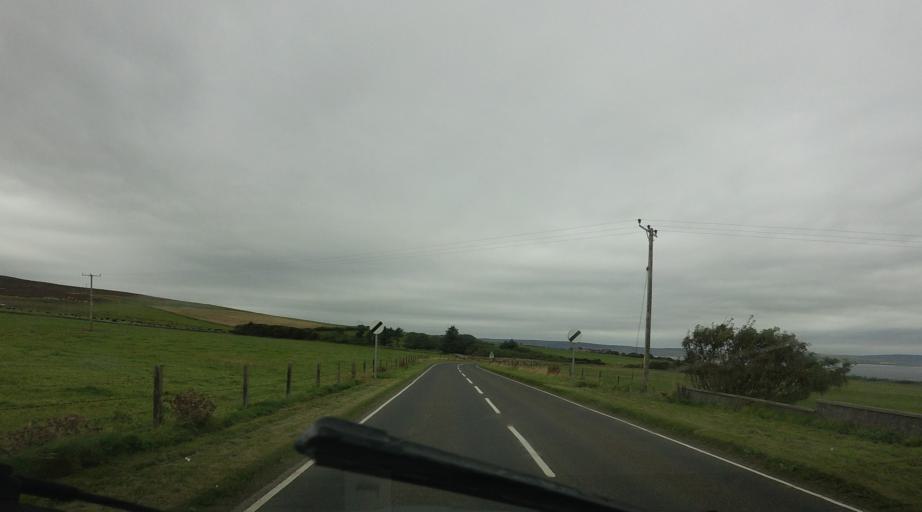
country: GB
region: Scotland
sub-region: Orkney Islands
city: Orkney
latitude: 58.9917
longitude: -2.9914
